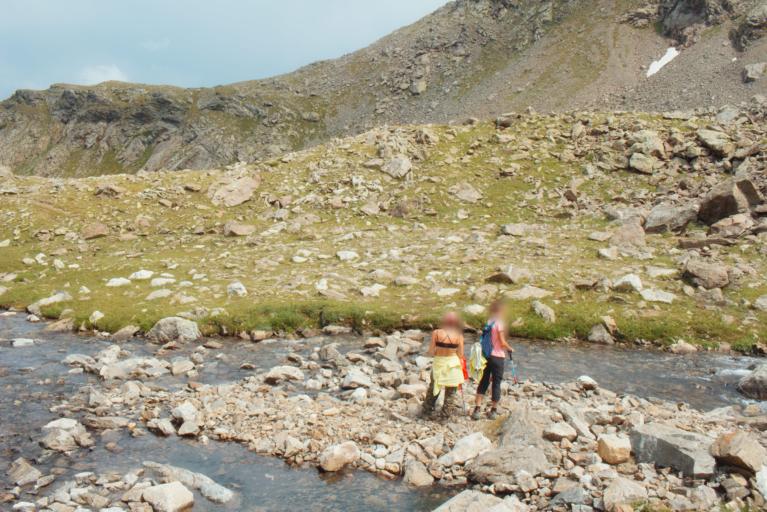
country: RU
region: Karachayevo-Cherkesiya
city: Nizhniy Arkhyz
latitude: 43.4509
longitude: 41.2355
